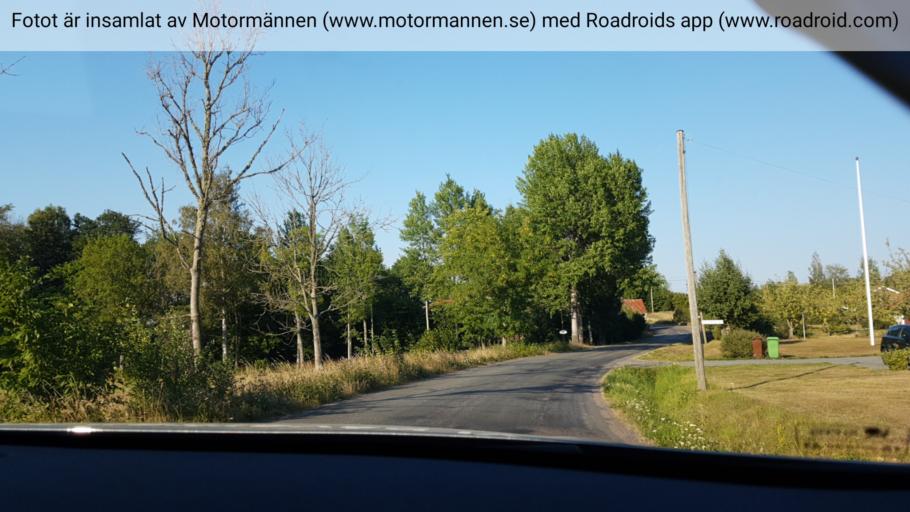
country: SE
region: Vaestra Goetaland
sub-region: Skovde Kommun
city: Stopen
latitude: 58.4828
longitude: 13.7545
